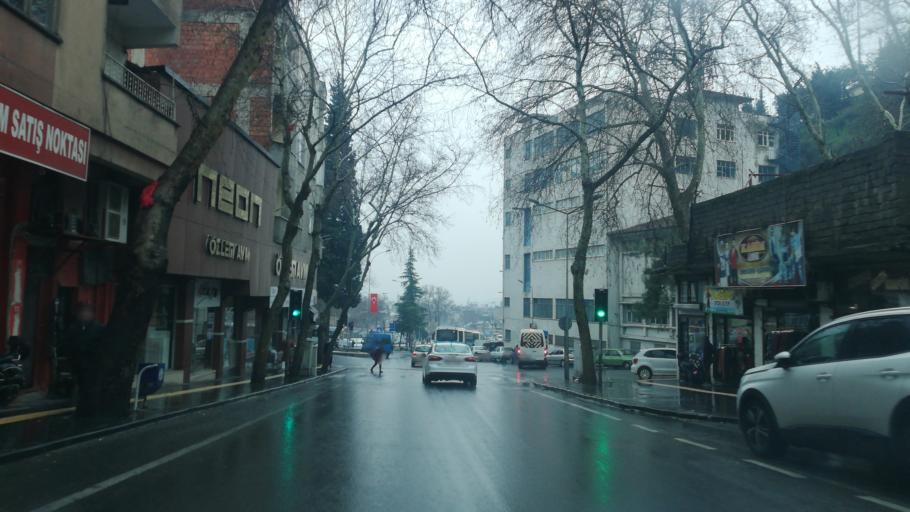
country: TR
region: Kahramanmaras
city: Kahramanmaras
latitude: 37.5874
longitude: 36.9270
